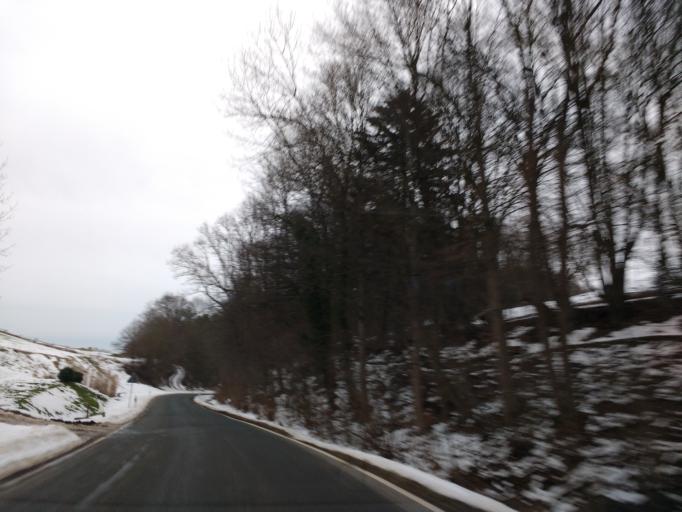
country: DE
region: Thuringia
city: Rohrberg
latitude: 51.4311
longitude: 10.0306
